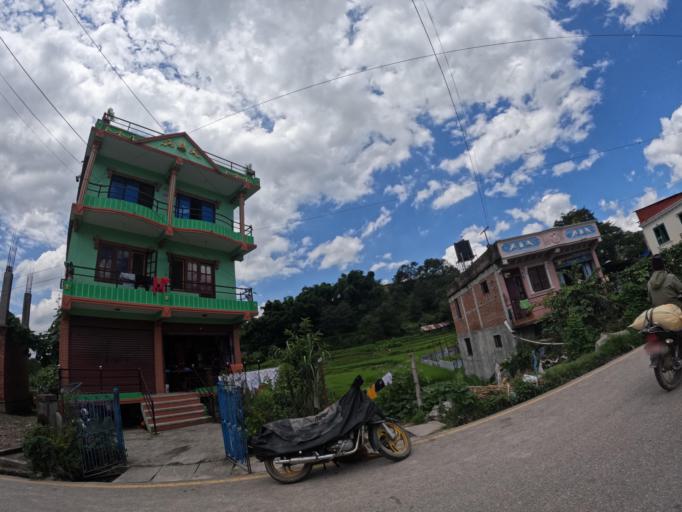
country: NP
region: Central Region
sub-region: Bagmati Zone
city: Kathmandu
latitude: 27.7728
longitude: 85.3303
